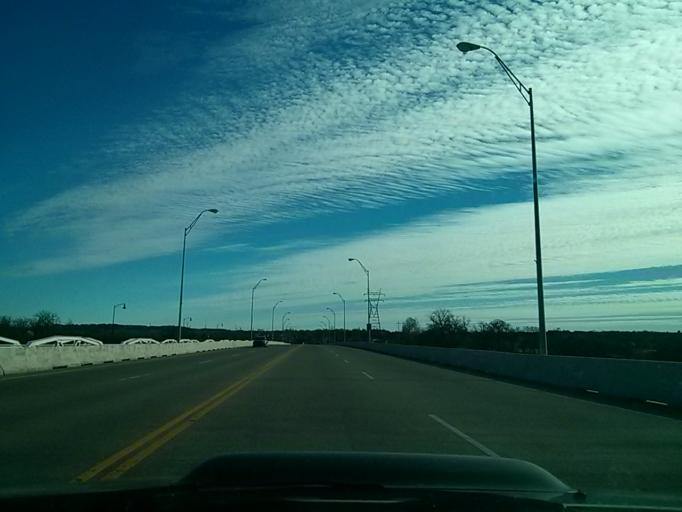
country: US
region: Oklahoma
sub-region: Tulsa County
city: Jenks
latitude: 36.0246
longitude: -95.9563
